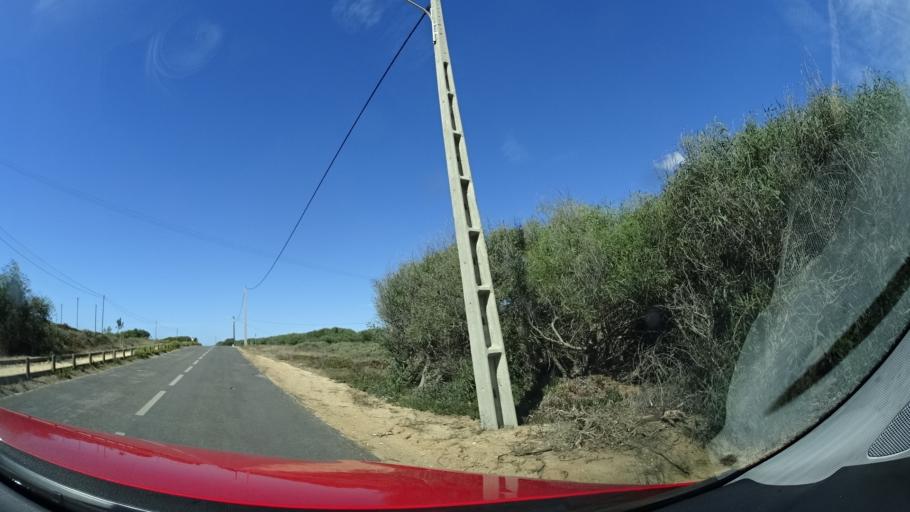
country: PT
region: Beja
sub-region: Odemira
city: Sao Teotonio
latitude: 37.5320
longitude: -8.7843
